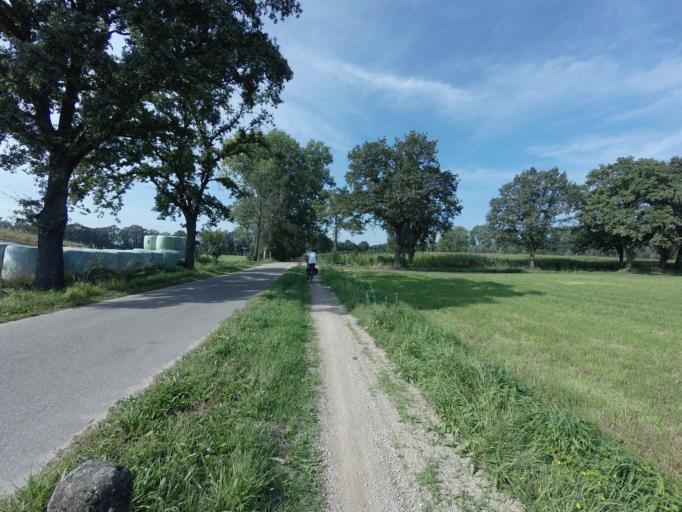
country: NL
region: Overijssel
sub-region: Gemeente Hof van Twente
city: Goor
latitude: 52.2581
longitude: 6.5969
